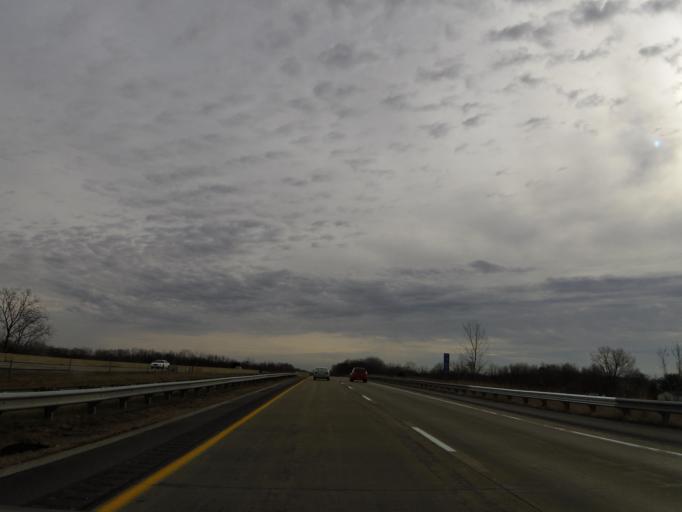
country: US
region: Indiana
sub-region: Marion County
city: Clermont
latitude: 39.8323
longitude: -86.3347
